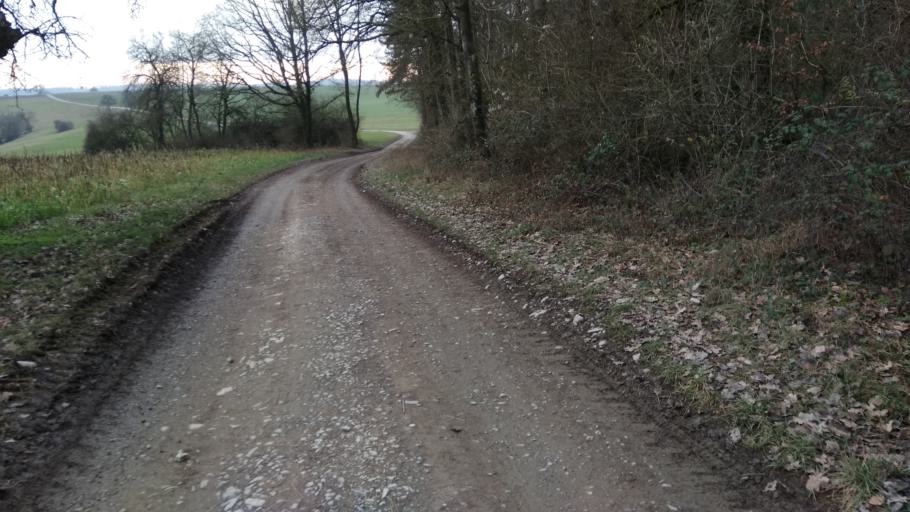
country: DE
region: Baden-Wuerttemberg
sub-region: Karlsruhe Region
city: Mosbach
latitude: 49.3630
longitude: 9.1747
